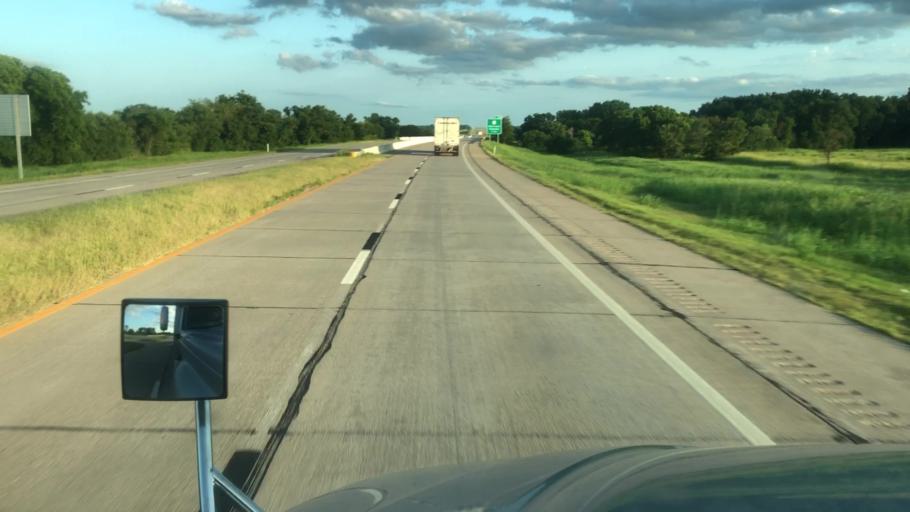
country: US
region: Oklahoma
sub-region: Pawnee County
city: Pawnee
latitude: 36.3124
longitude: -96.9926
